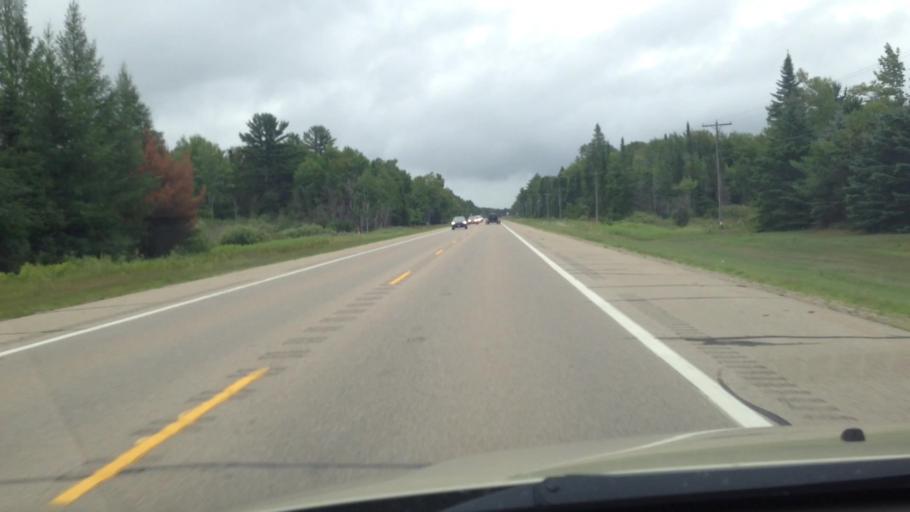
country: US
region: Michigan
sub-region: Delta County
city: Gladstone
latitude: 45.8955
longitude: -86.7233
